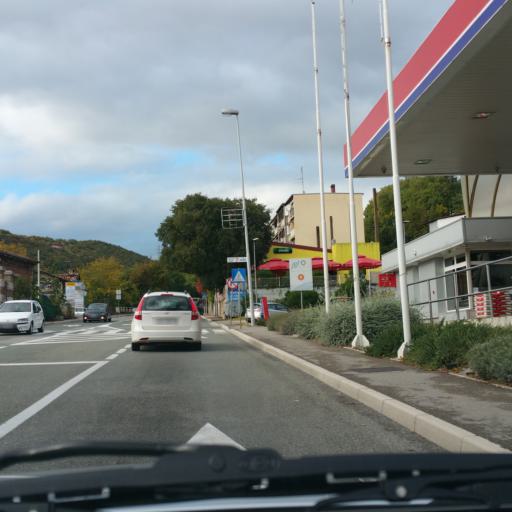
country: HR
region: Primorsko-Goranska
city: Drenova
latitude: 45.3417
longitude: 14.4252
